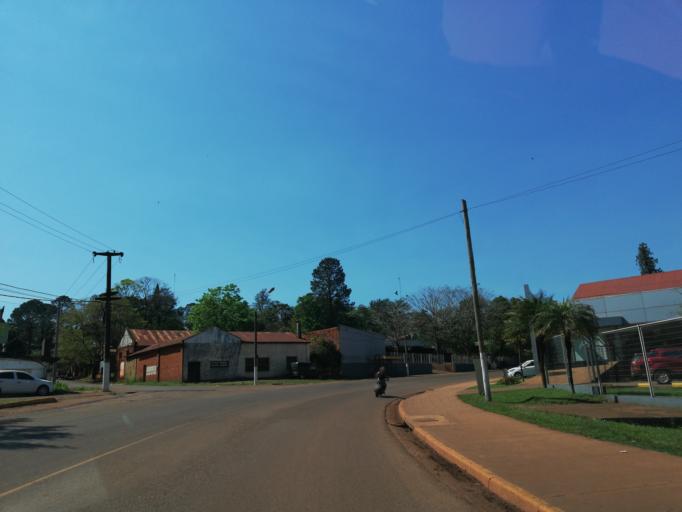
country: AR
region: Misiones
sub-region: Departamento de Eldorado
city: Eldorado
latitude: -26.4066
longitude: -54.6475
